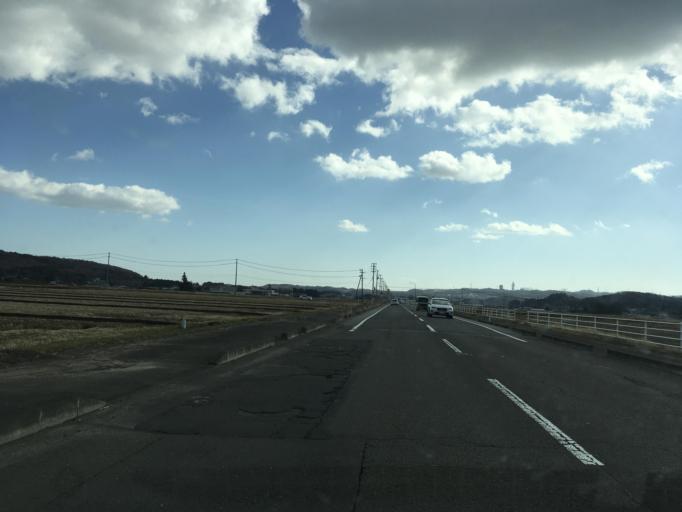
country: JP
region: Miyagi
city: Tomiya
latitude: 38.3469
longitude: 140.7854
